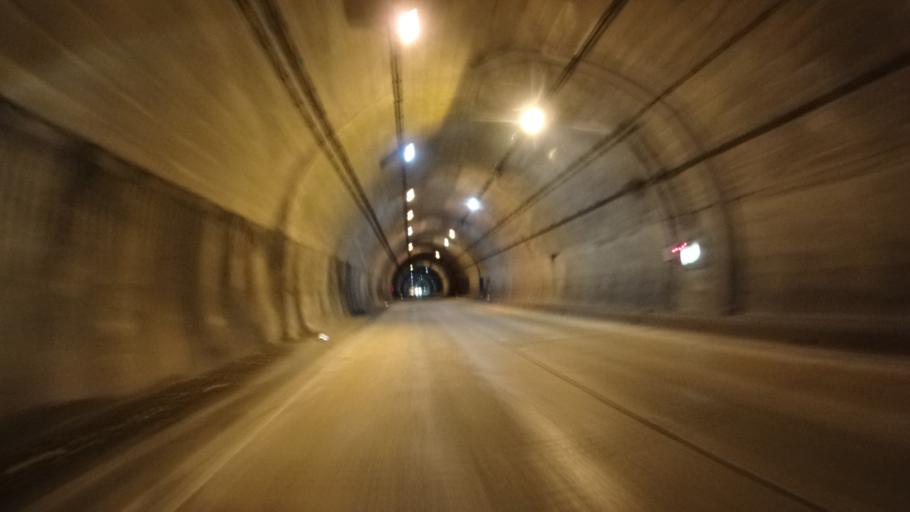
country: JP
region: Ishikawa
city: Tsurugi-asahimachi
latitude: 36.3698
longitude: 136.5845
